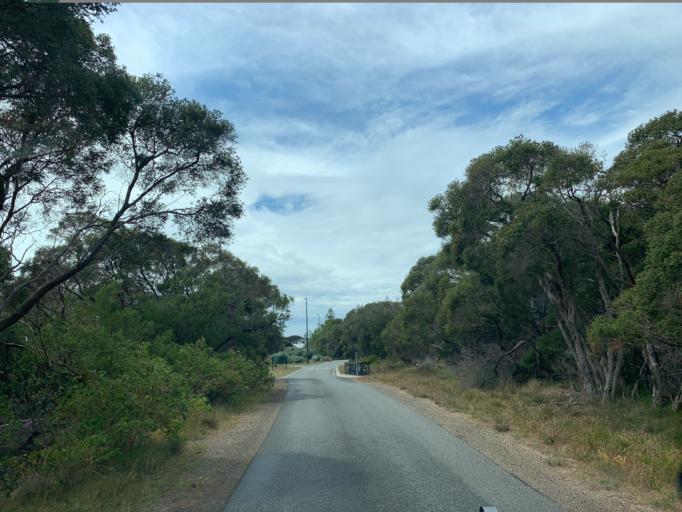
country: AU
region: Victoria
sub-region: Queenscliffe
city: Queenscliff
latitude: -38.3141
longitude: 144.6909
